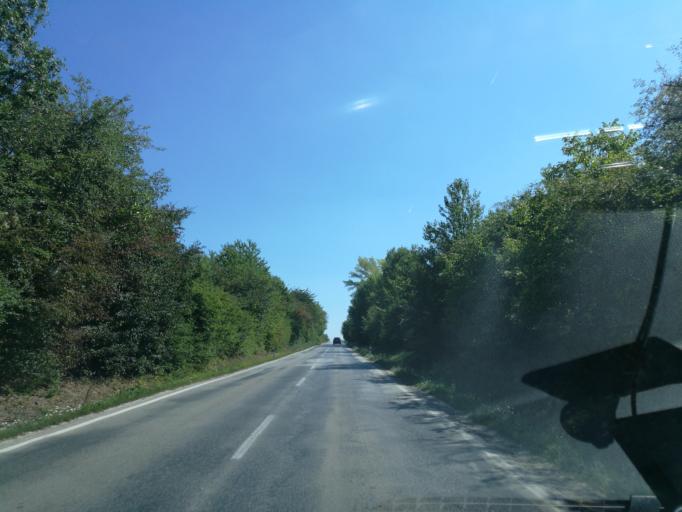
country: SK
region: Trnavsky
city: Vrbove
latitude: 48.6412
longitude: 17.7071
